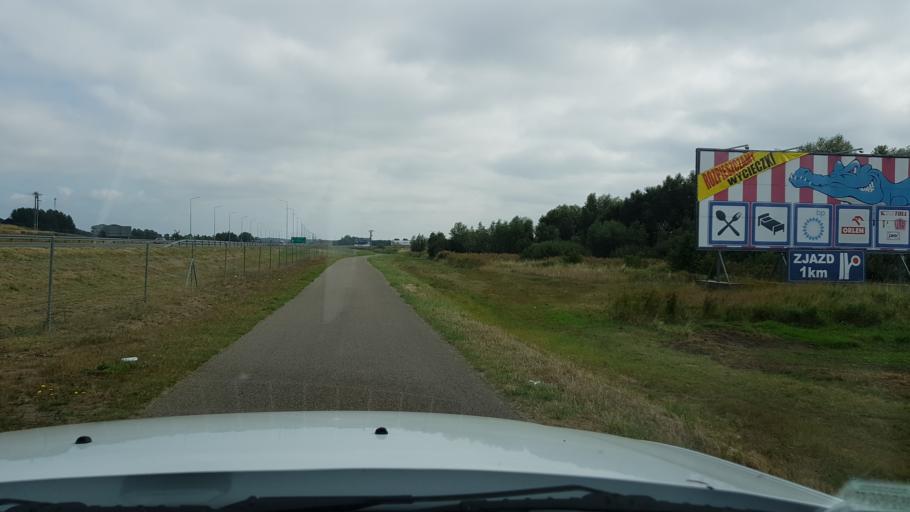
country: PL
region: West Pomeranian Voivodeship
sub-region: Powiat pyrzycki
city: Lipiany
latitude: 52.9569
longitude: 14.9342
